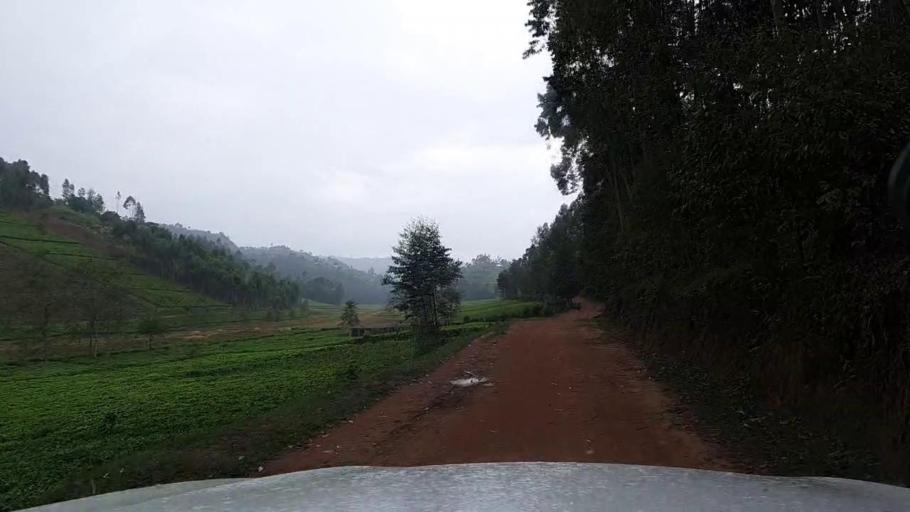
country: RW
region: Northern Province
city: Byumba
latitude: -1.6515
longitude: 29.9346
